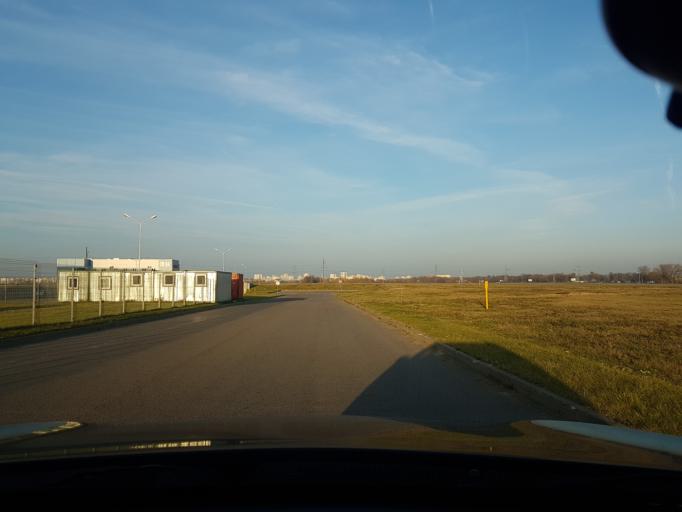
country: BY
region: Minsk
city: Shchomyslitsa
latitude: 53.8251
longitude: 27.4350
